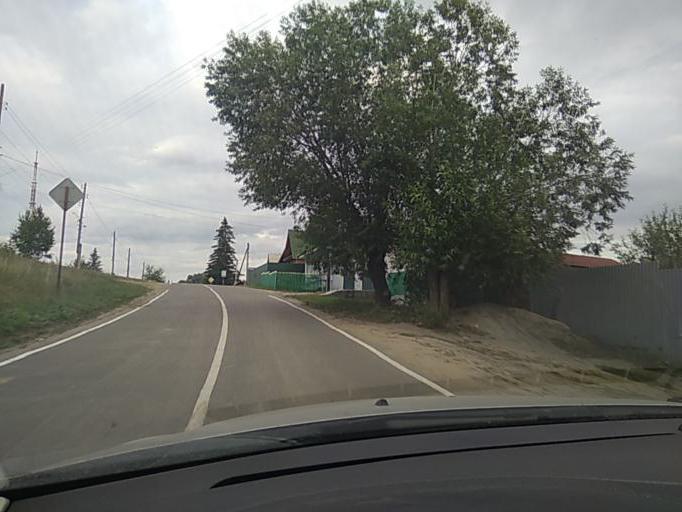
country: RU
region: Chelyabinsk
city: Kyshtym
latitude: 55.6940
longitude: 60.5446
